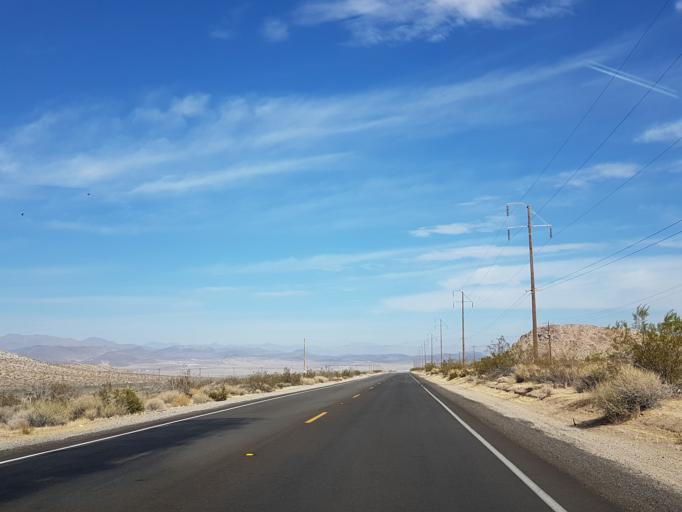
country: US
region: California
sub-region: Kern County
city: Ridgecrest
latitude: 35.6300
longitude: -117.5836
